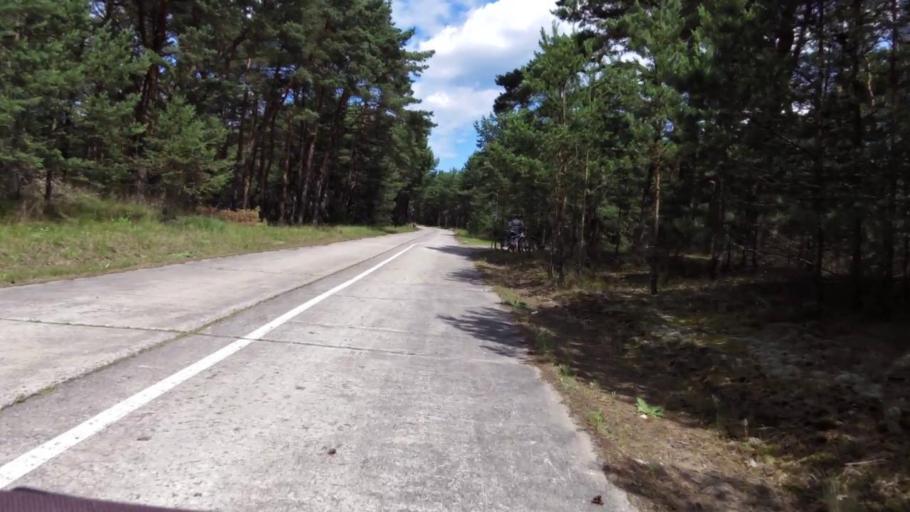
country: PL
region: West Pomeranian Voivodeship
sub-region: Powiat gryficki
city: Mrzezyno
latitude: 54.1249
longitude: 15.2363
